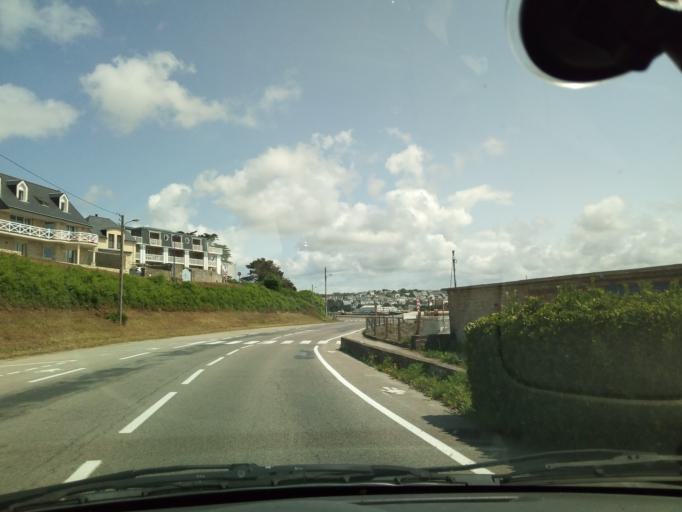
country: FR
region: Brittany
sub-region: Departement du Finistere
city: Audierne
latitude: 48.0131
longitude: -4.5410
